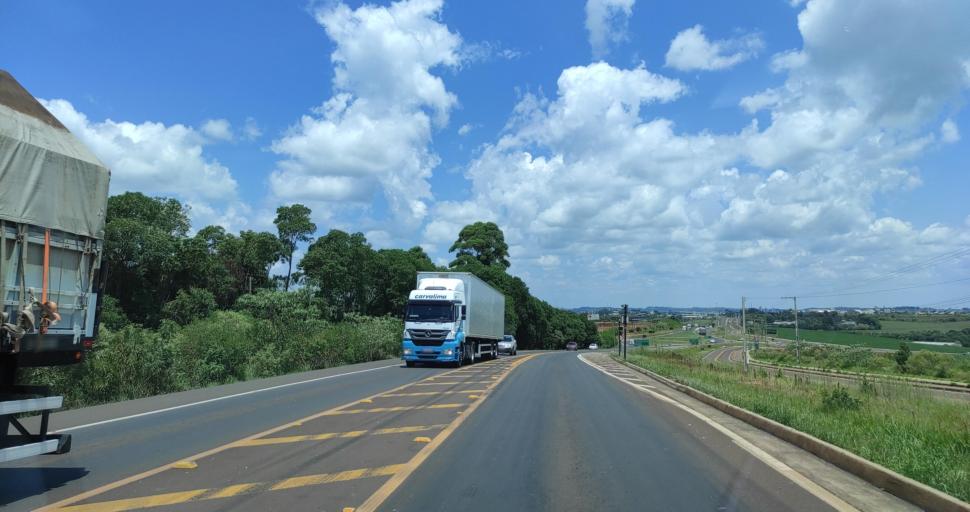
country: BR
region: Santa Catarina
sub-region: Xanxere
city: Xanxere
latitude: -26.8802
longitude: -52.3554
